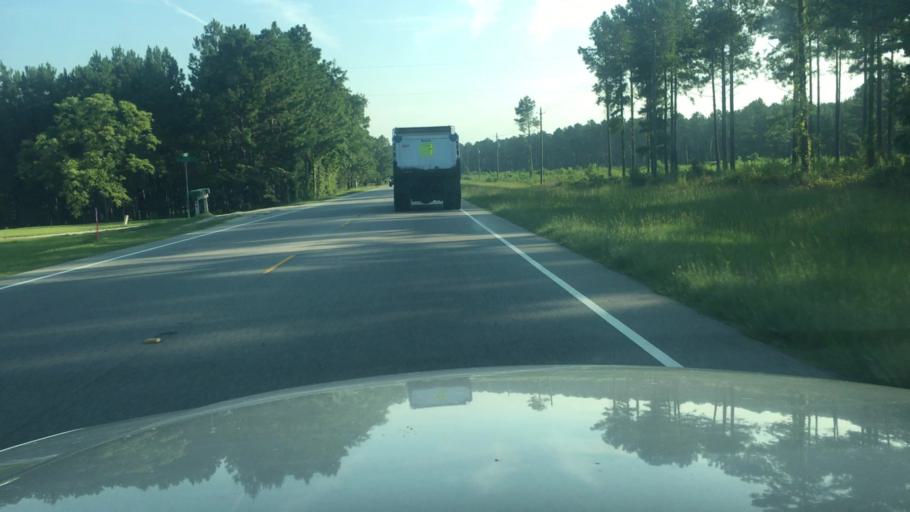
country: US
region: North Carolina
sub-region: Harnett County
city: Walkertown
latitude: 35.1897
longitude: -78.8511
